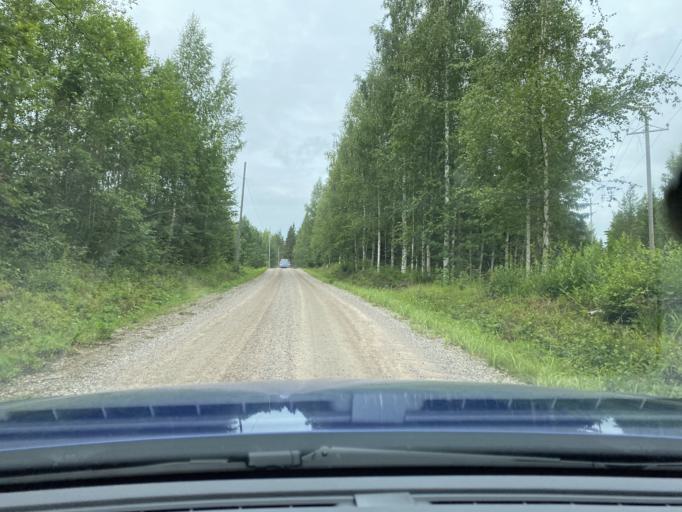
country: FI
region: Pirkanmaa
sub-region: Ylae-Pirkanmaa
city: Maenttae
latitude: 62.0216
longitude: 24.7310
